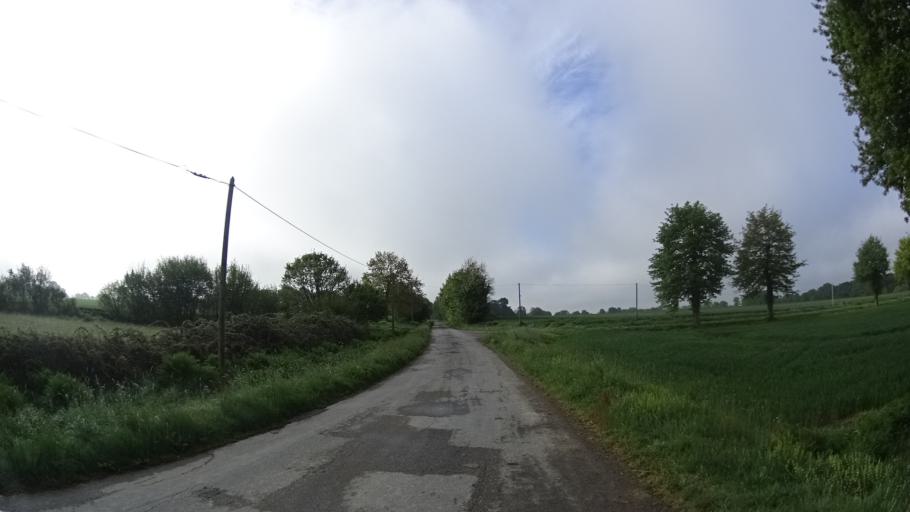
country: FR
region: Brittany
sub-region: Departement d'Ille-et-Vilaine
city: Mordelles
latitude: 48.0903
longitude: -1.8564
